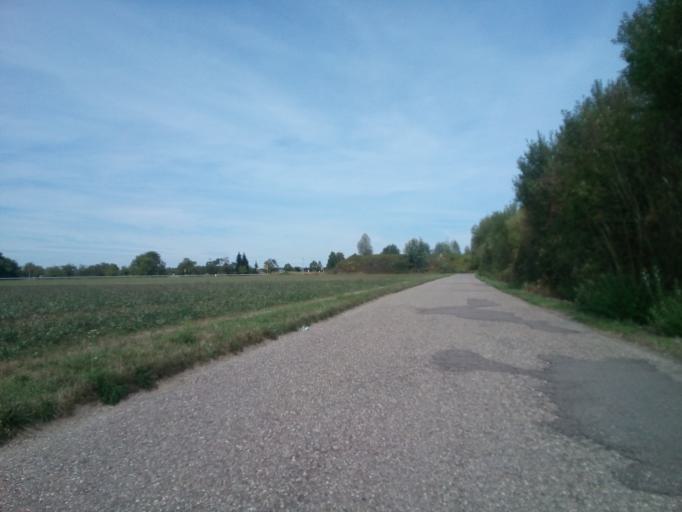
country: DE
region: Baden-Wuerttemberg
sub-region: Karlsruhe Region
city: Sinzheim
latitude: 48.7569
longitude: 8.1554
